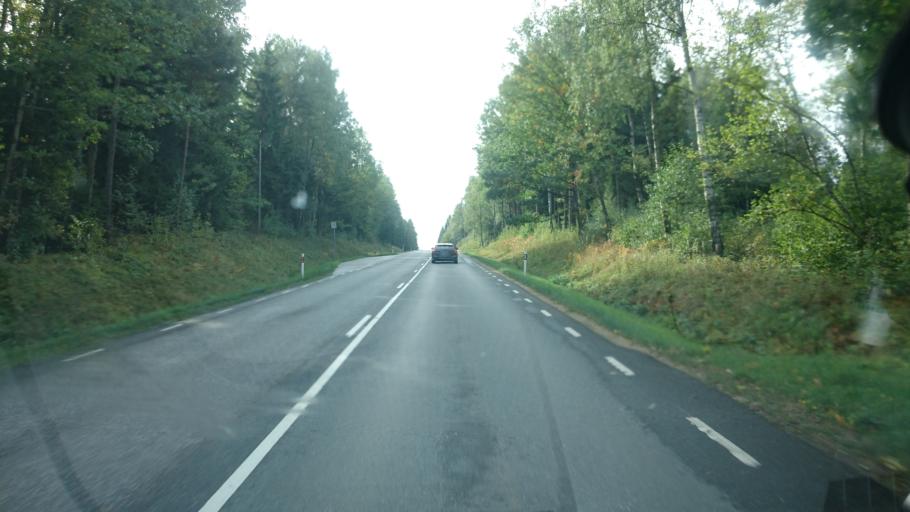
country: SE
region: Vaestra Goetaland
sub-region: Alingsas Kommun
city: Sollebrunn
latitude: 58.0306
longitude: 12.4631
